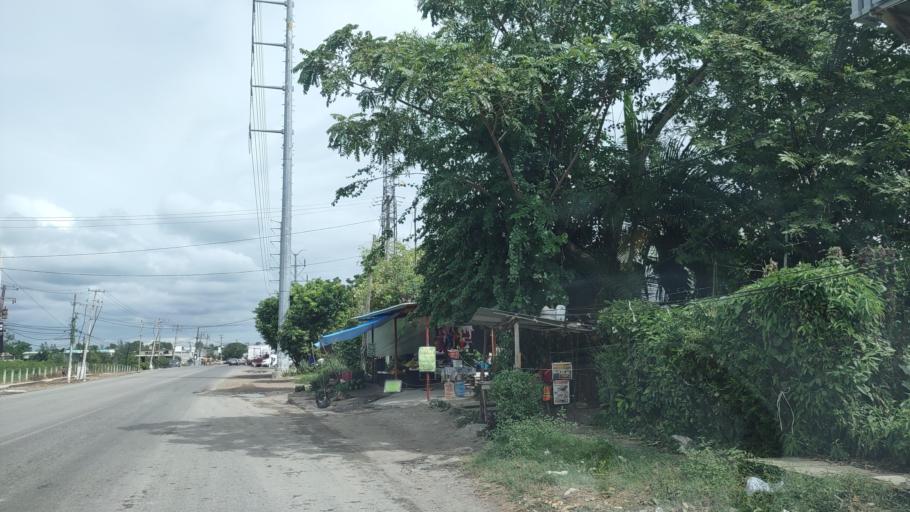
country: MX
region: Veracruz
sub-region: Papantla
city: Residencial Tajin
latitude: 20.5921
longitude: -97.4224
